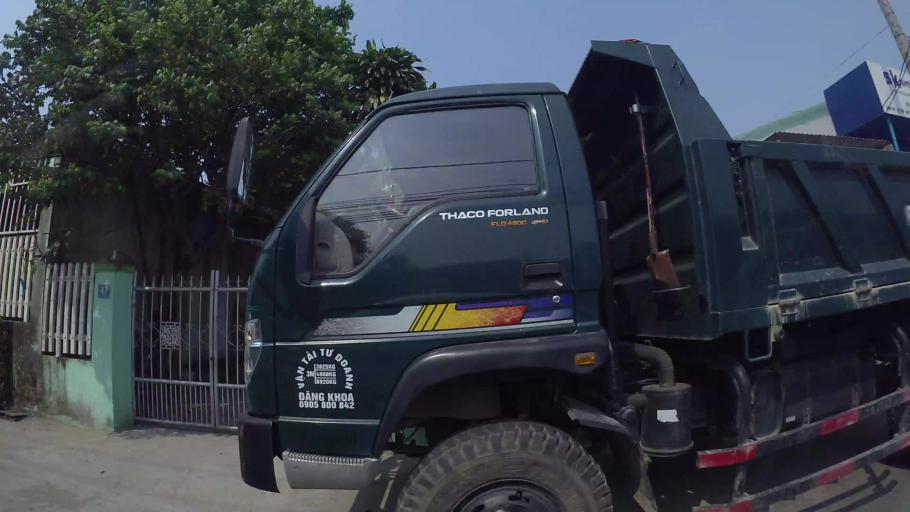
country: VN
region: Da Nang
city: Ngu Hanh Son
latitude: 15.9894
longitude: 108.2405
